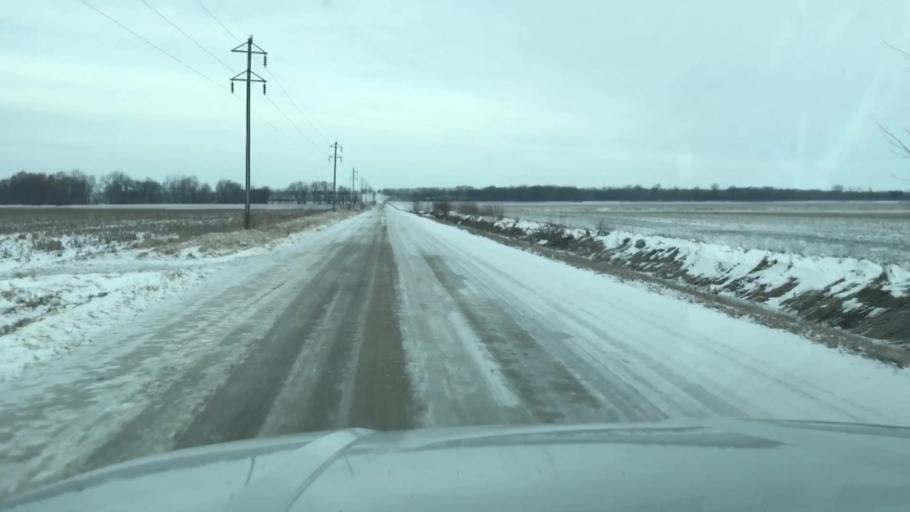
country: US
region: Missouri
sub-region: Holt County
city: Oregon
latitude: 40.1300
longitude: -95.0337
